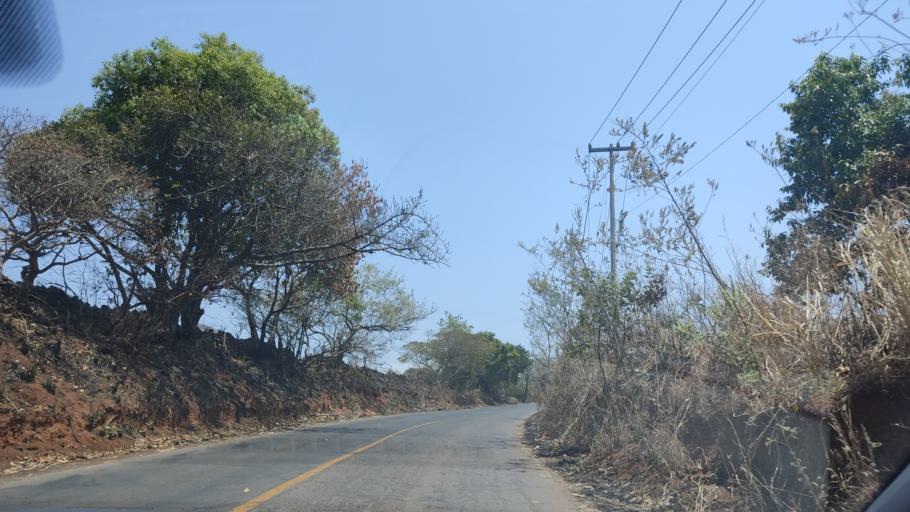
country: MX
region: Nayarit
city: Puga
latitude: 21.5878
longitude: -104.8068
